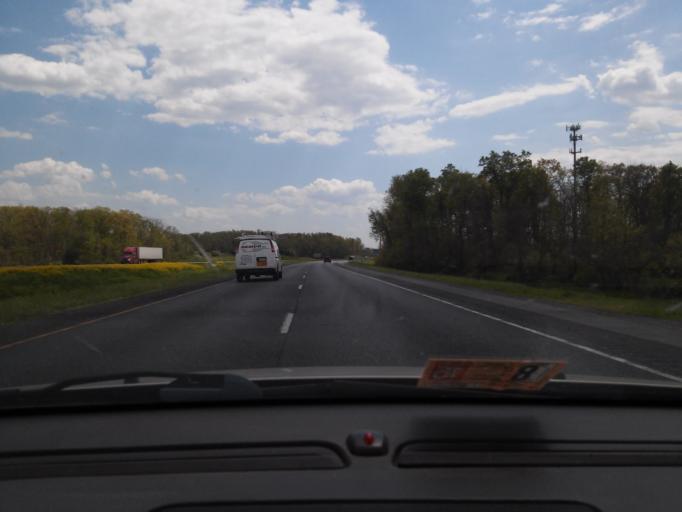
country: US
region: Virginia
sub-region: City of Winchester
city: Winchester
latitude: 39.1971
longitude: -78.1343
